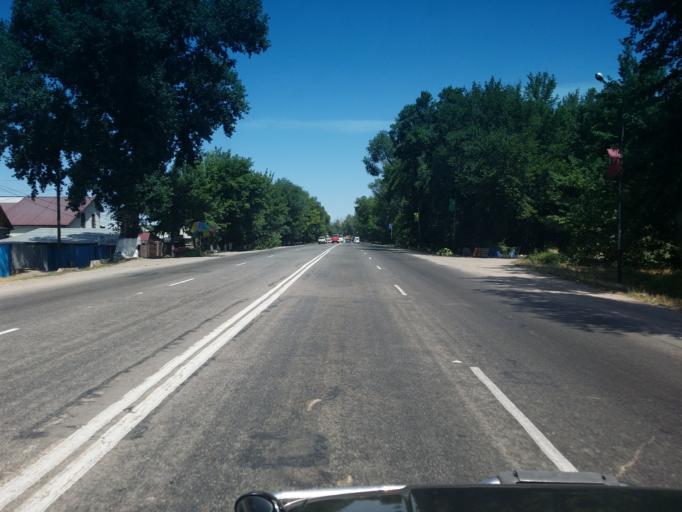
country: KZ
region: Almaty Oblysy
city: Energeticheskiy
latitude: 43.3436
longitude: 77.0512
